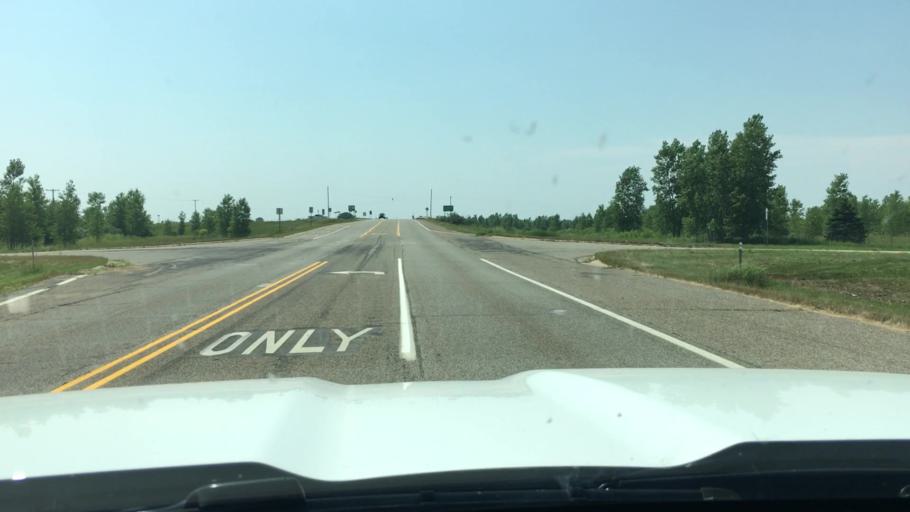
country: US
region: Michigan
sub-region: Gratiot County
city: Ithaca
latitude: 43.1760
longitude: -84.5577
